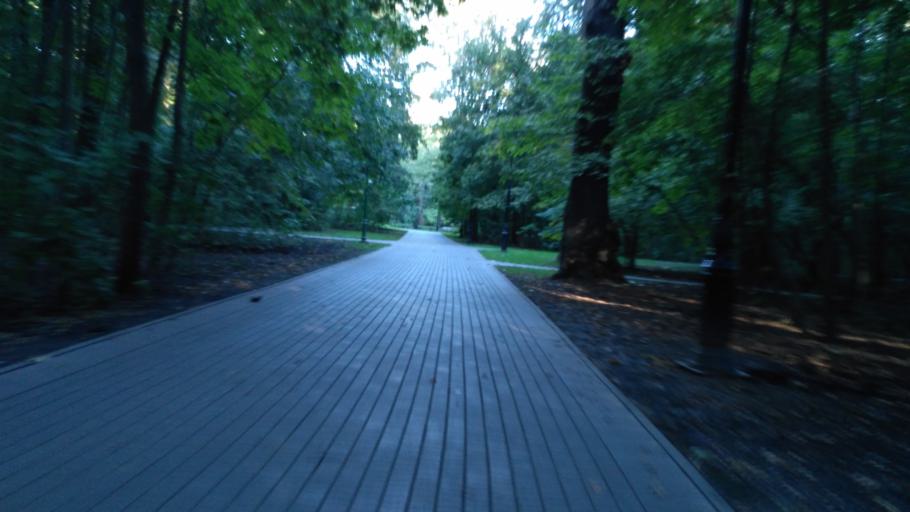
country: RU
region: Moscow
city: Ostankinskiy
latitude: 55.8280
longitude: 37.6085
